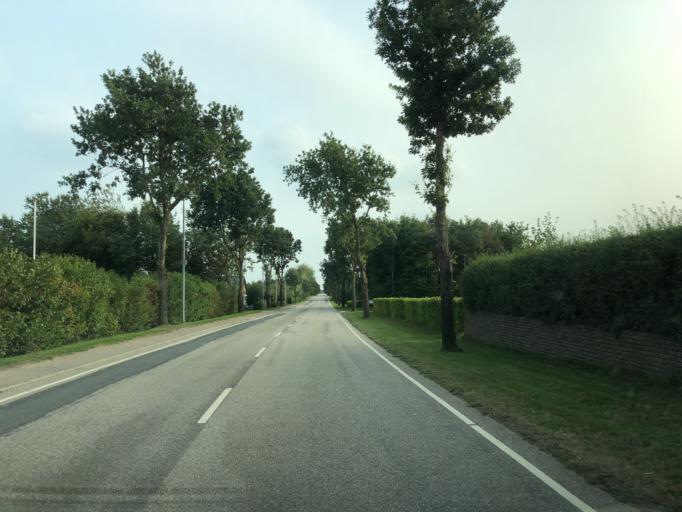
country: DK
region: Central Jutland
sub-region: Ringkobing-Skjern Kommune
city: Videbaek
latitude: 56.0970
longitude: 8.7027
